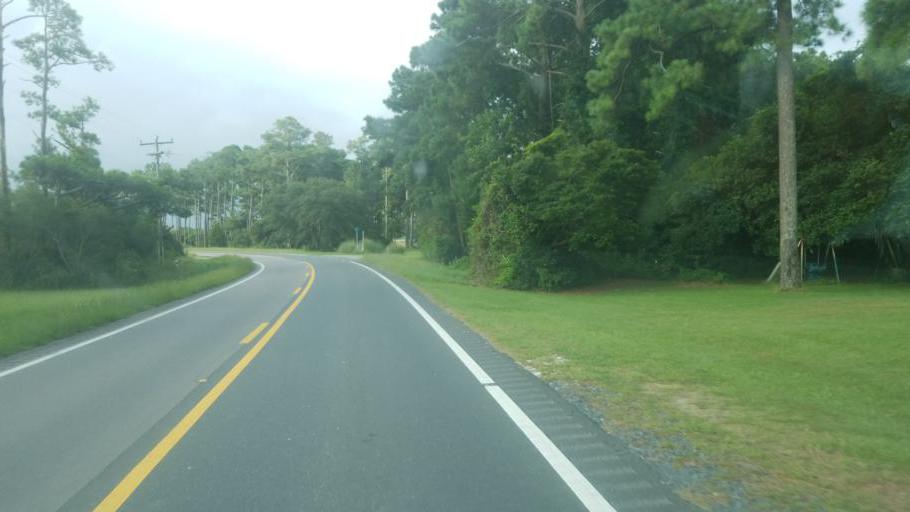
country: US
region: North Carolina
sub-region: Dare County
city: Manteo
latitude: 35.8810
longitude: -75.6596
